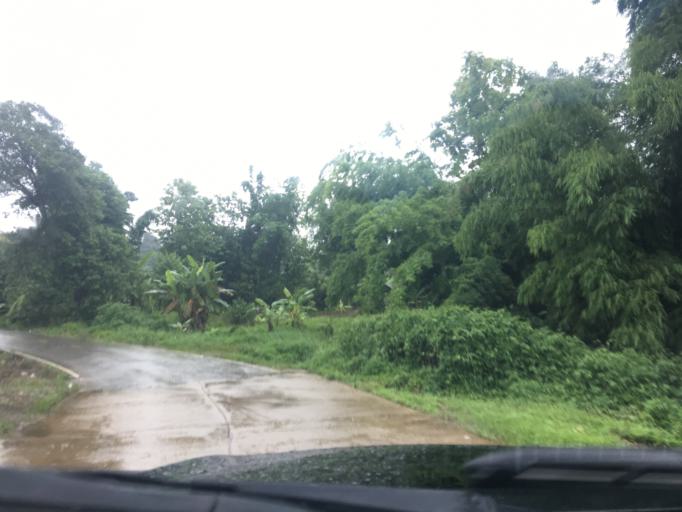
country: TH
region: Chiang Rai
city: Chiang Khong
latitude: 20.2996
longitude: 100.2530
